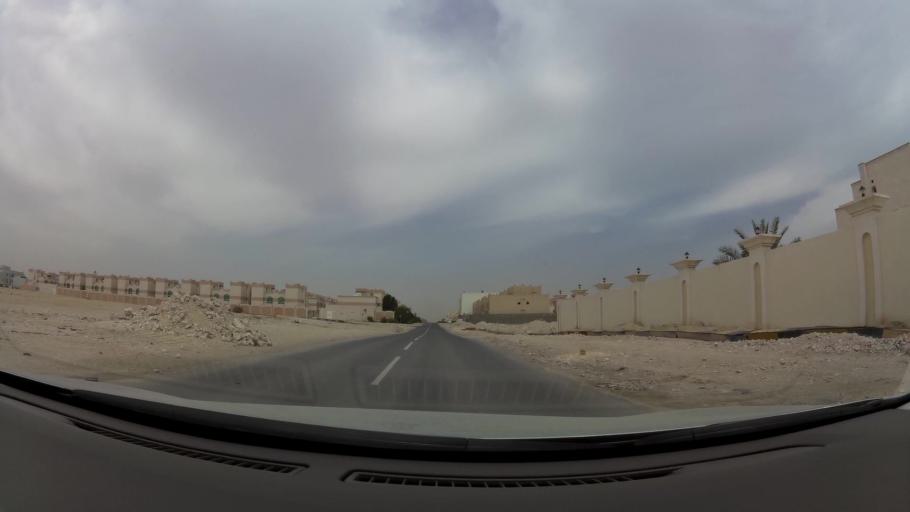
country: QA
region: Baladiyat ar Rayyan
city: Ar Rayyan
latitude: 25.2880
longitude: 51.4560
